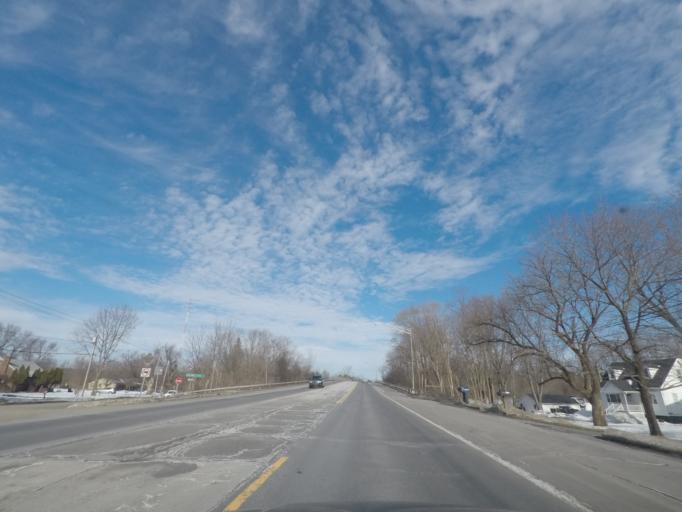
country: US
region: New York
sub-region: Schenectady County
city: Rotterdam
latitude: 42.7853
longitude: -74.0161
